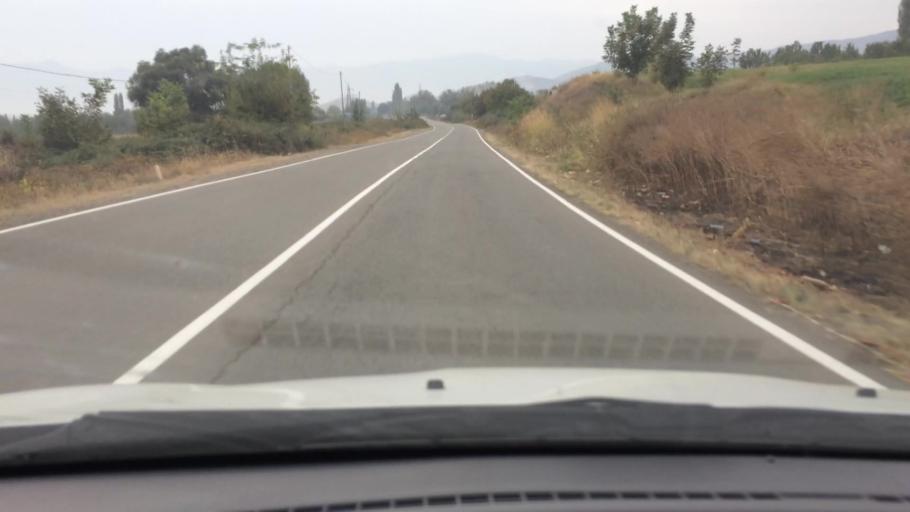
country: GE
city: Naghvarevi
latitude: 41.3134
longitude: 44.7930
